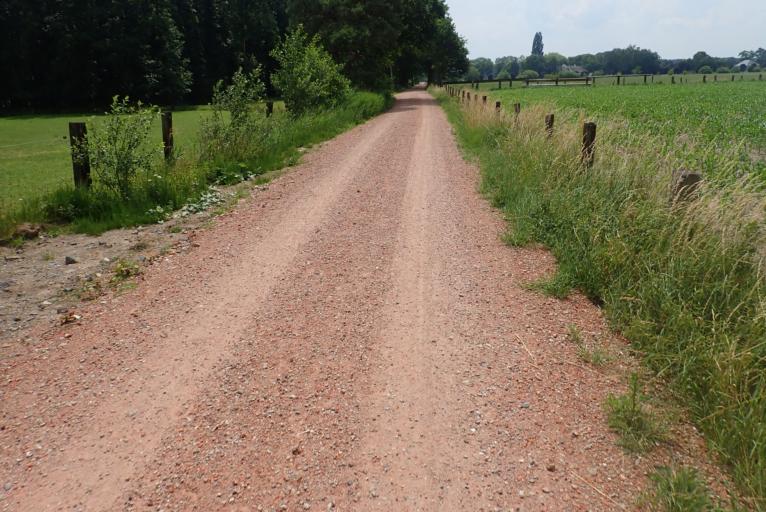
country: BE
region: Flanders
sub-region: Provincie Antwerpen
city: Brecht
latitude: 51.3067
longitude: 4.6419
